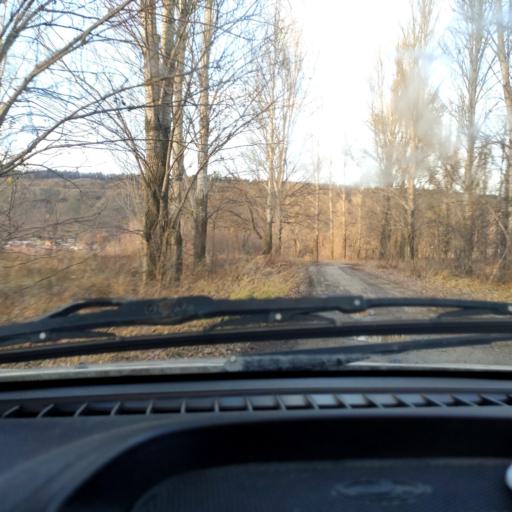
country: RU
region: Samara
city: Povolzhskiy
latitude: 53.4669
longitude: 49.6861
